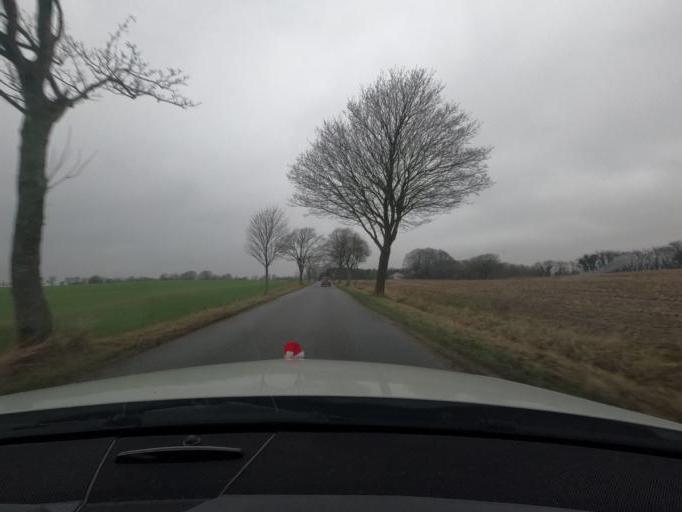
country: DK
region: South Denmark
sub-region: Haderslev Kommune
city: Haderslev
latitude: 55.1934
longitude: 9.4895
